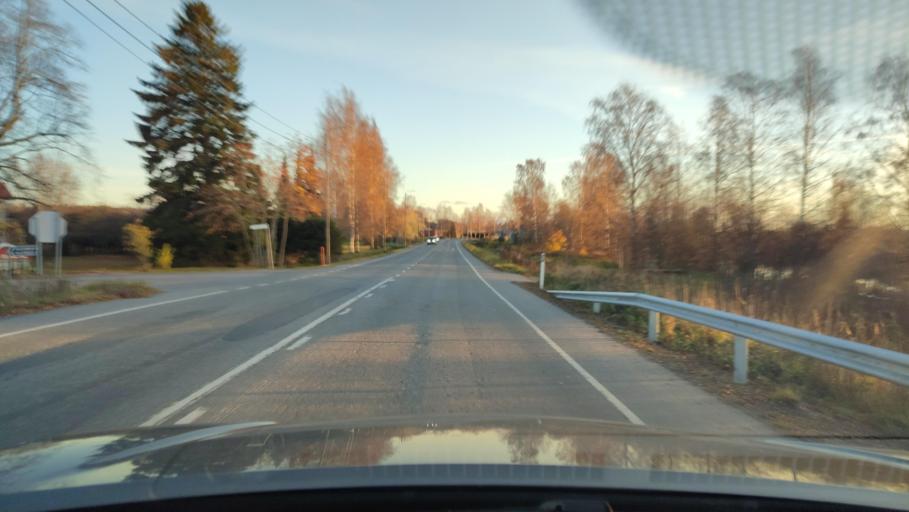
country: FI
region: Ostrobothnia
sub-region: Sydosterbotten
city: Naerpes
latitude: 62.4639
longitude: 21.3555
